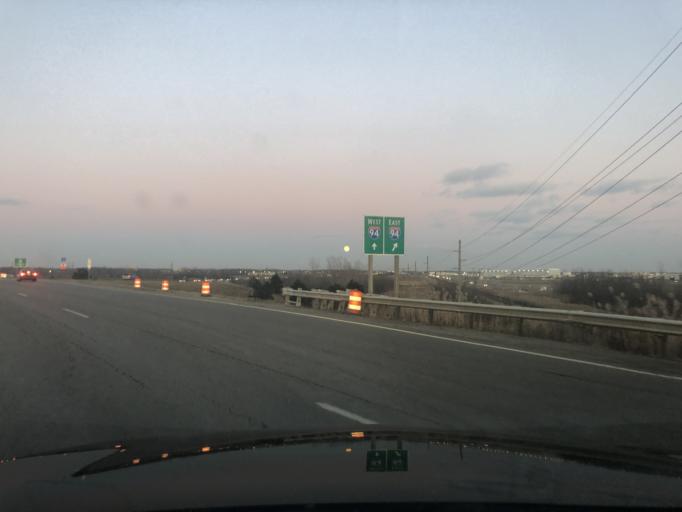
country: US
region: Michigan
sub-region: Wayne County
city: Romulus
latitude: 42.2300
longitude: -83.3698
